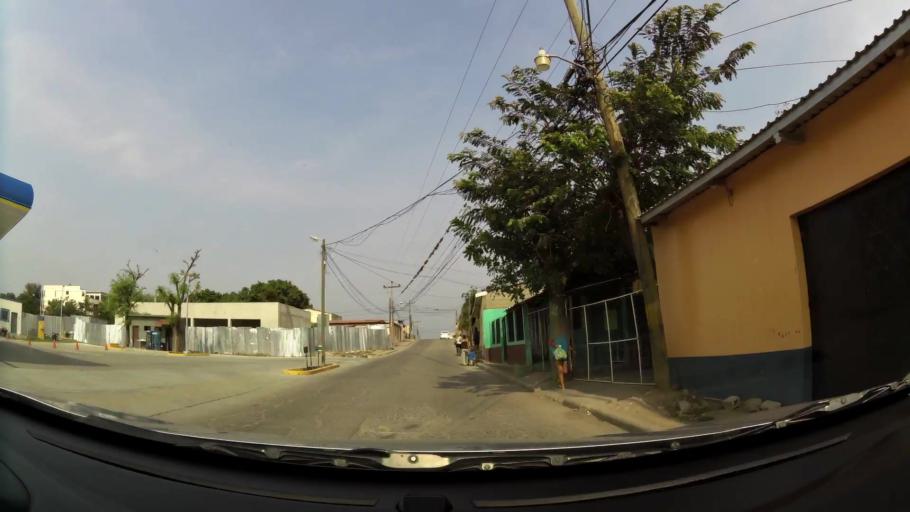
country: HN
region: Comayagua
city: Comayagua
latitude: 14.4569
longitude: -87.6292
